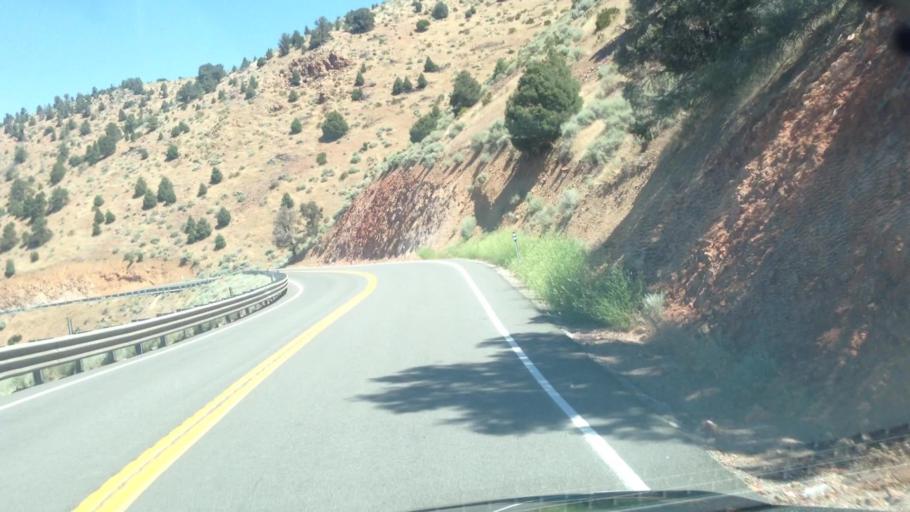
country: US
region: Nevada
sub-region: Storey County
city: Virginia City
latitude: 39.3791
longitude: -119.6959
